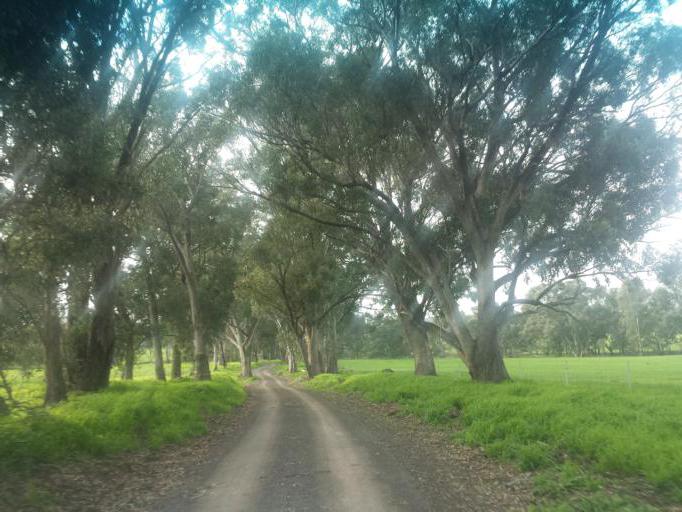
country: AU
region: Victoria
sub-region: Murrindindi
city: Kinglake West
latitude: -37.0407
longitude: 145.2502
